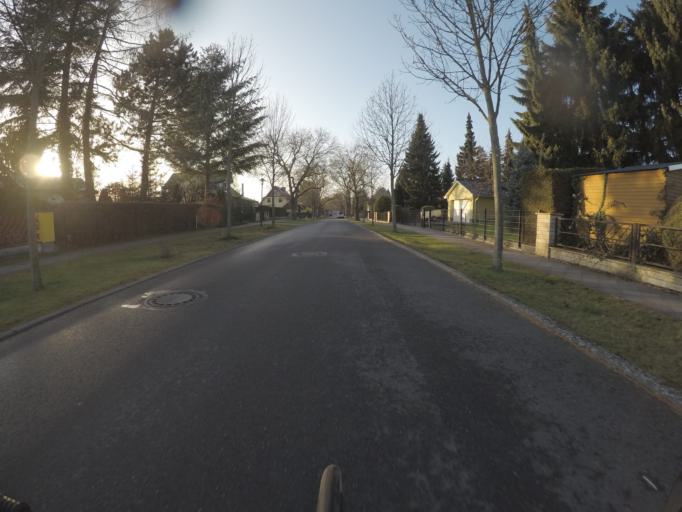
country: DE
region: Brandenburg
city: Birkenwerder
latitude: 52.6913
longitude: 13.2707
